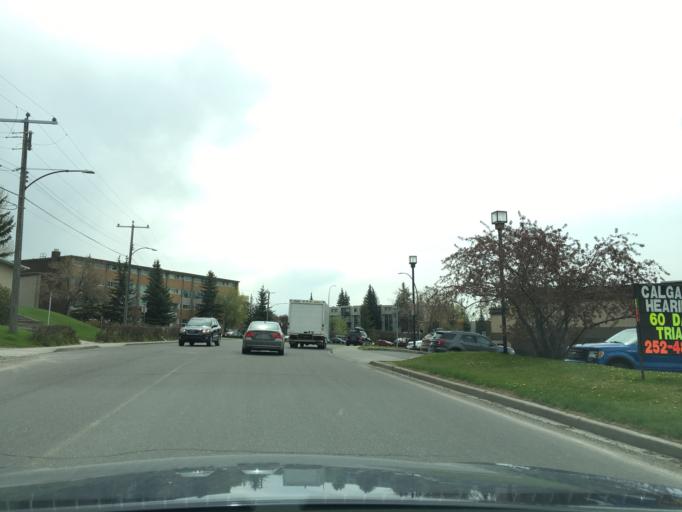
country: CA
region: Alberta
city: Calgary
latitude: 50.9808
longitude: -114.0684
